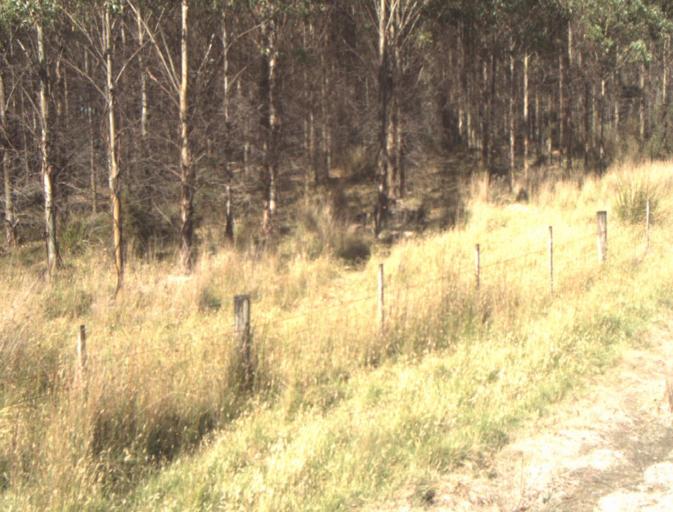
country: AU
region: Tasmania
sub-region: Launceston
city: Newstead
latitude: -41.3053
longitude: 147.3127
